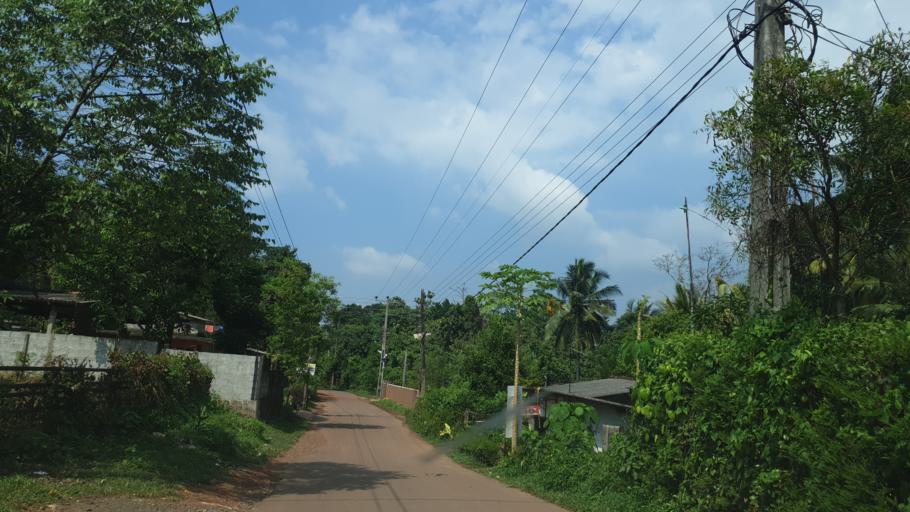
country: LK
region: Western
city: Panadura
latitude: 6.7322
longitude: 79.9530
